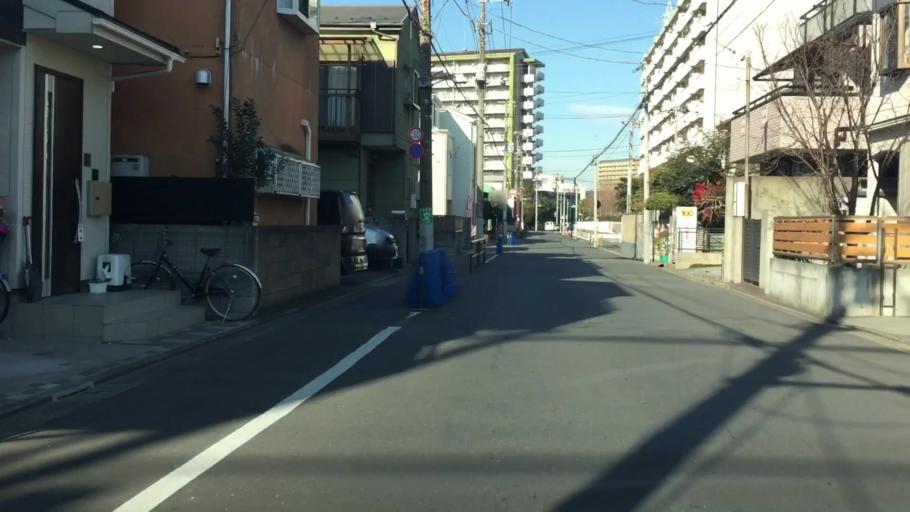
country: JP
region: Saitama
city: Kawaguchi
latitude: 35.7713
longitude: 139.7406
